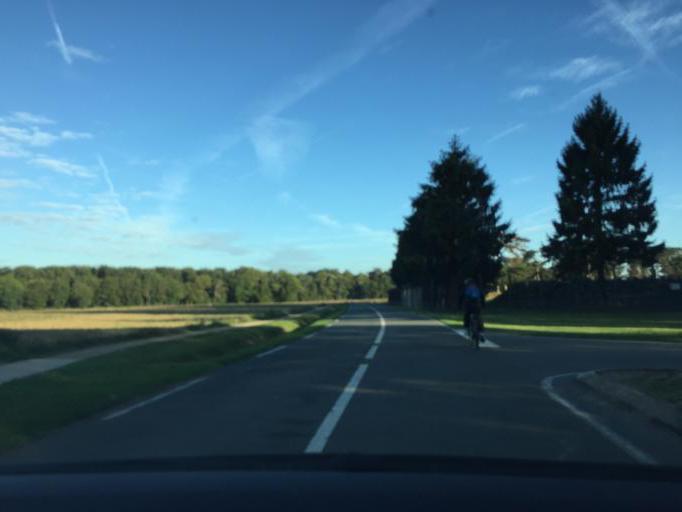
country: FR
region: Ile-de-France
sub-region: Departement de l'Essonne
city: Villiers-le-Bacle
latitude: 48.7201
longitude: 2.1380
